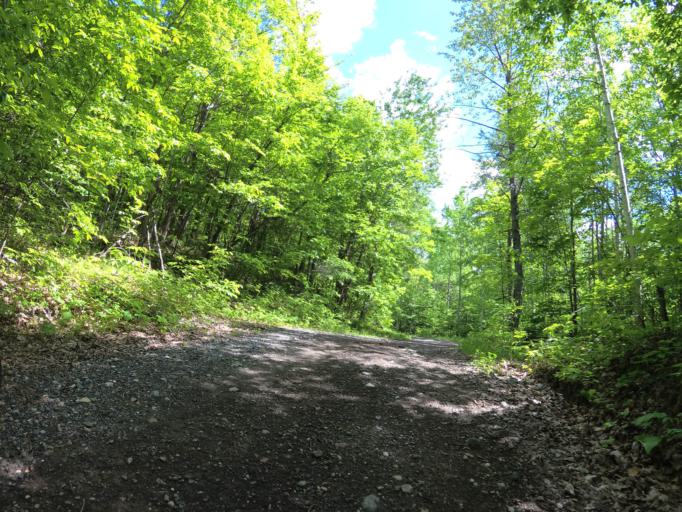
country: CA
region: Ontario
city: Renfrew
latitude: 45.0803
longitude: -76.7657
